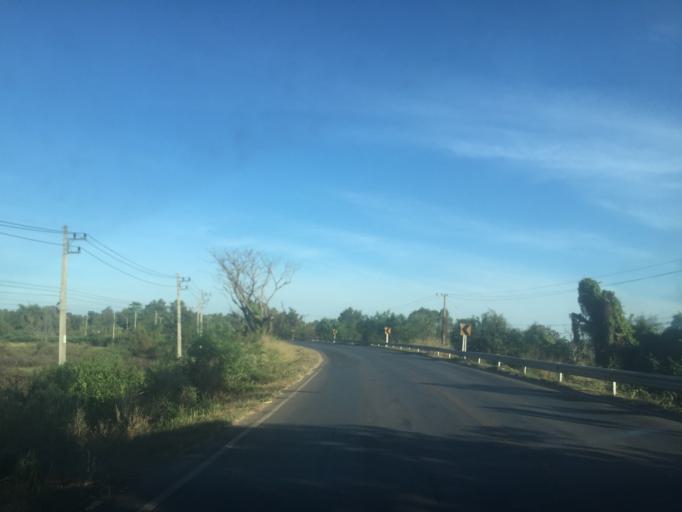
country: TH
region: Kalasin
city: Tha Khantho
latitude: 16.9621
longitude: 103.2545
